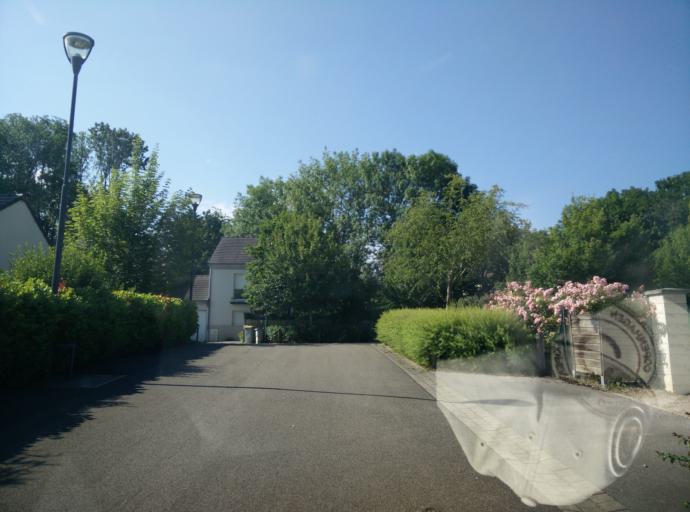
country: FR
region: Franche-Comte
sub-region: Departement du Doubs
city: Besancon
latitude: 47.2624
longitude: 6.0241
